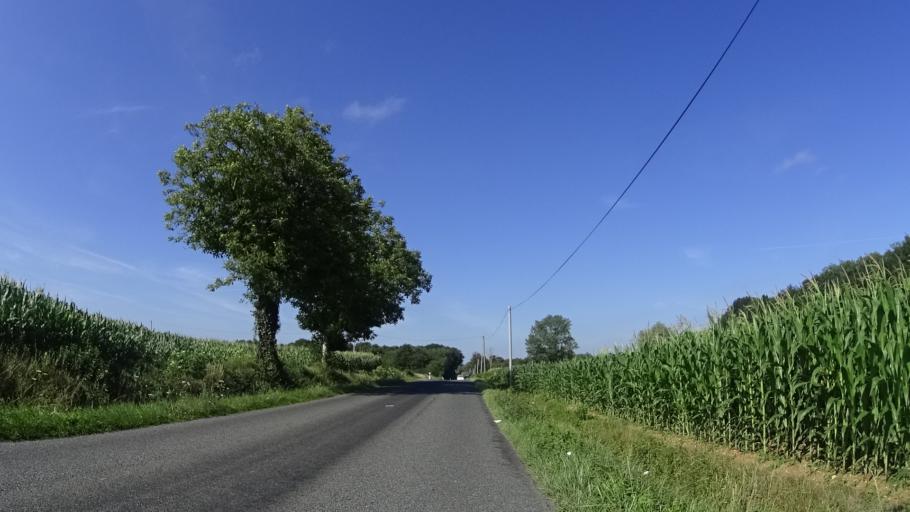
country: FR
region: Pays de la Loire
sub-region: Departement de Maine-et-Loire
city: Etriche
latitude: 47.6335
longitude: -0.4349
